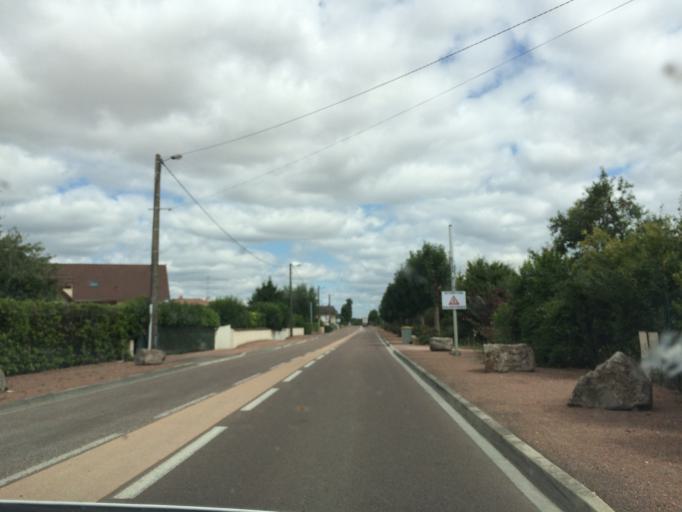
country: FR
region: Bourgogne
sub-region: Departement de la Cote-d'Or
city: Fenay
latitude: 47.2397
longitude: 5.0585
